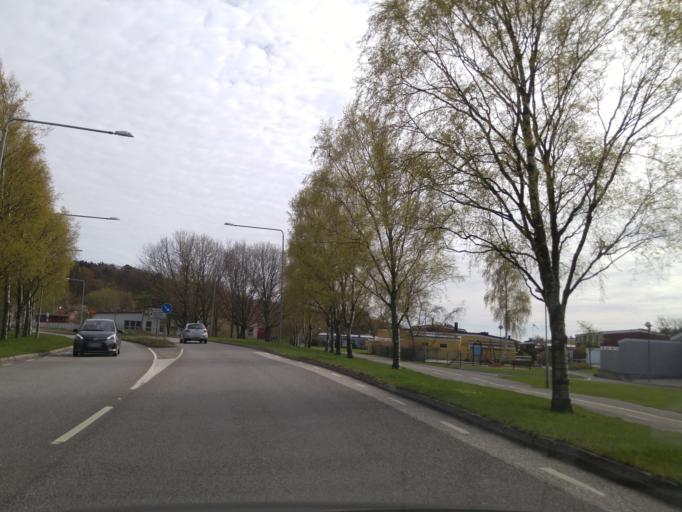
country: SE
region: Vaestra Goetaland
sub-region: Goteborg
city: Majorna
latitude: 57.6563
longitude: 11.8702
